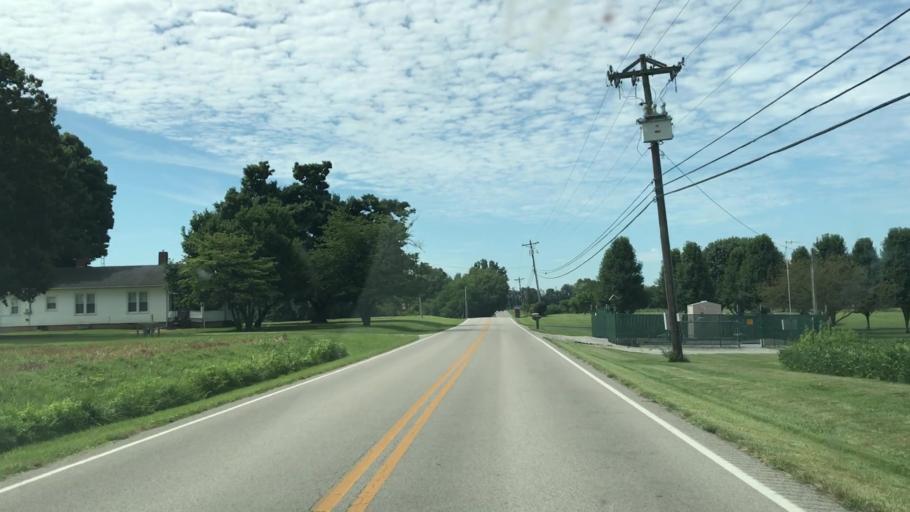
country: US
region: Kentucky
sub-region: Edmonson County
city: Brownsville
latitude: 37.0652
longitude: -86.2114
